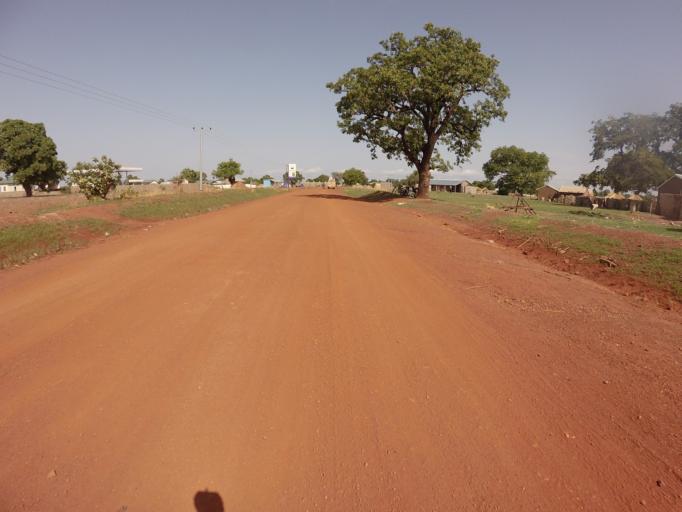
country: GH
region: Upper East
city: Bawku
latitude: 10.8313
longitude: -0.1707
